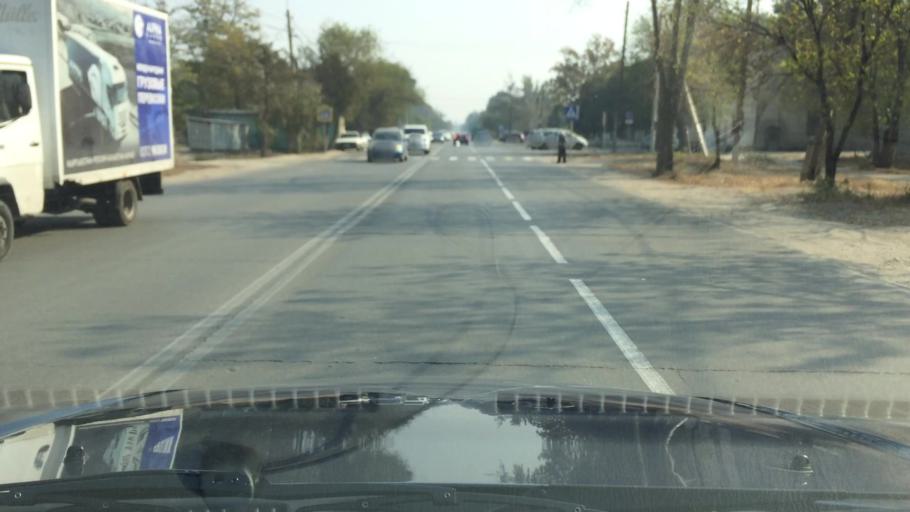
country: KG
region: Chuy
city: Lebedinovka
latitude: 42.8836
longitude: 74.6391
